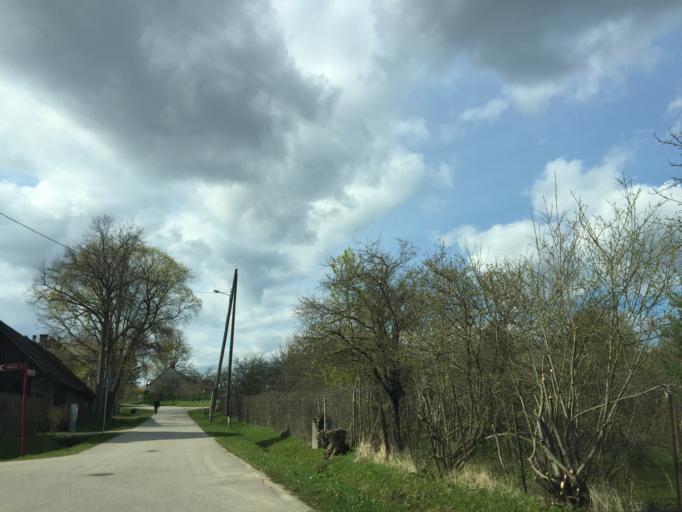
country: LV
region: Plavinu
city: Plavinas
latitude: 56.6177
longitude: 25.7147
